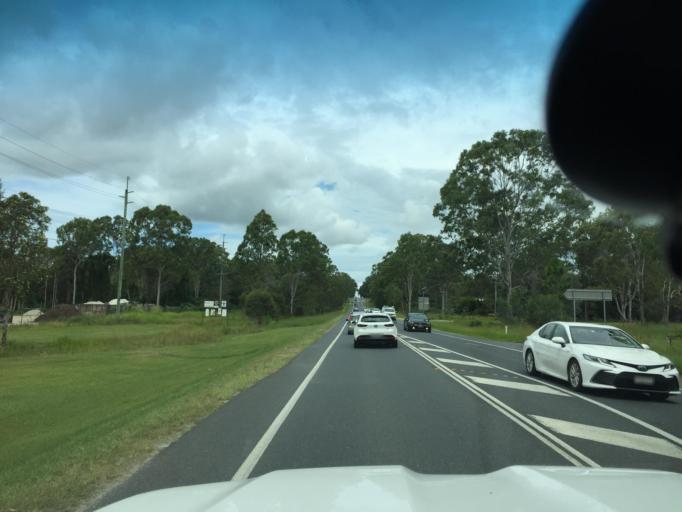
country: AU
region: Queensland
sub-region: Moreton Bay
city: Deception Bay
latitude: -27.1818
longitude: 152.9971
